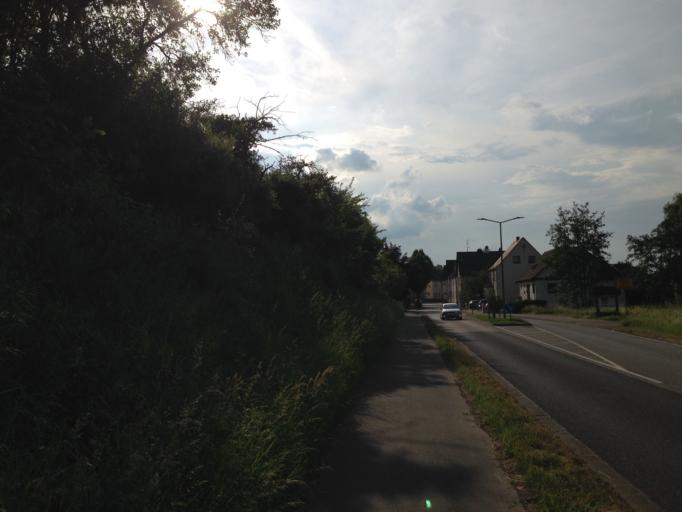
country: DE
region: Hesse
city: Allendorf an der Lahn
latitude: 50.5476
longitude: 8.6215
